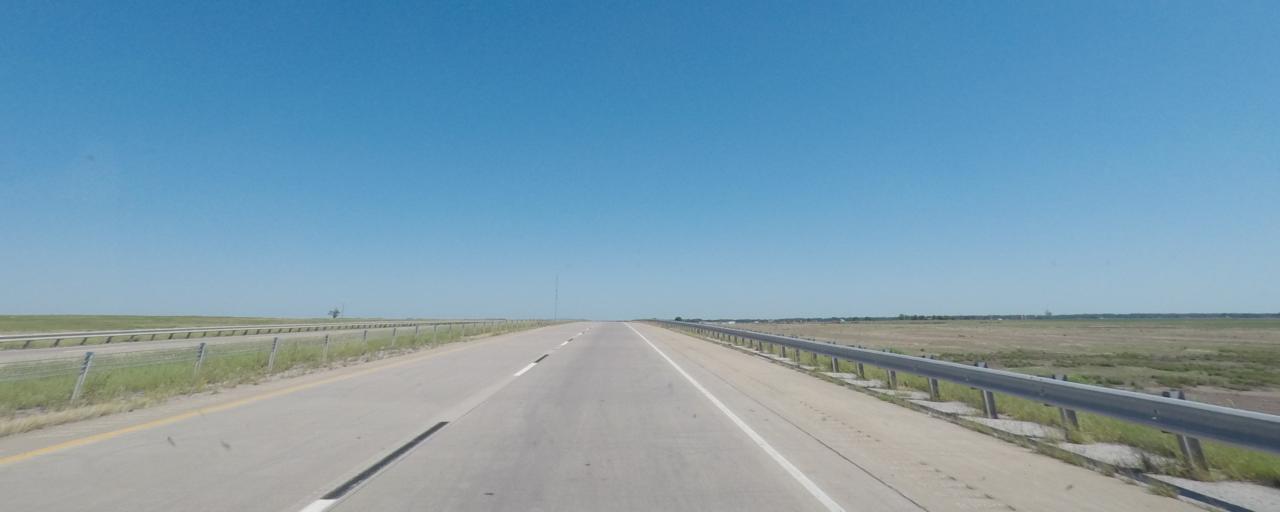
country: US
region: Oklahoma
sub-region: Kay County
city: Tonkawa
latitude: 36.6283
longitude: -97.3457
